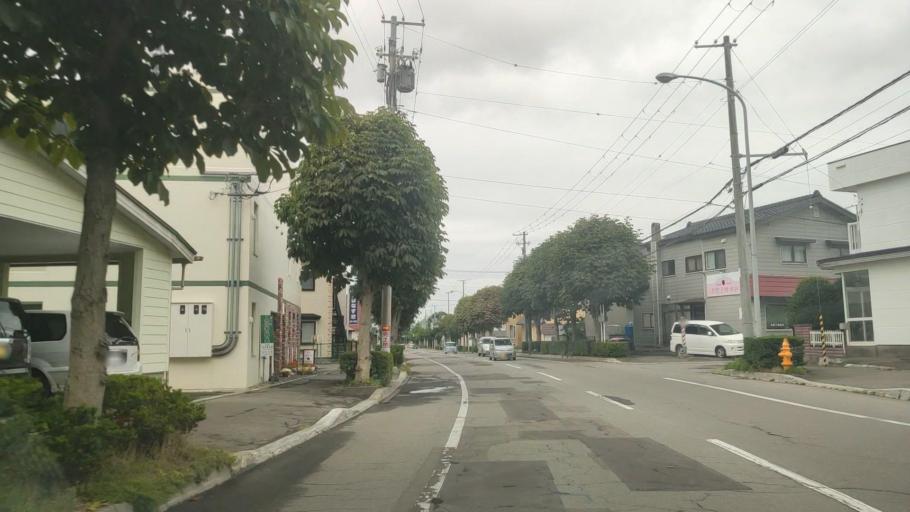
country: JP
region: Hokkaido
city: Hakodate
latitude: 41.7978
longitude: 140.7617
